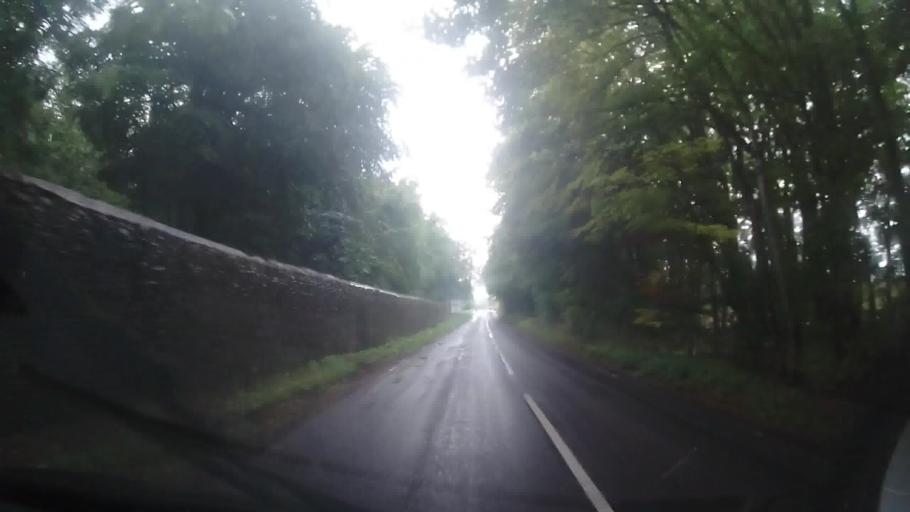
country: GB
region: England
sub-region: Oxfordshire
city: Woodstock
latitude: 51.8669
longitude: -1.3838
